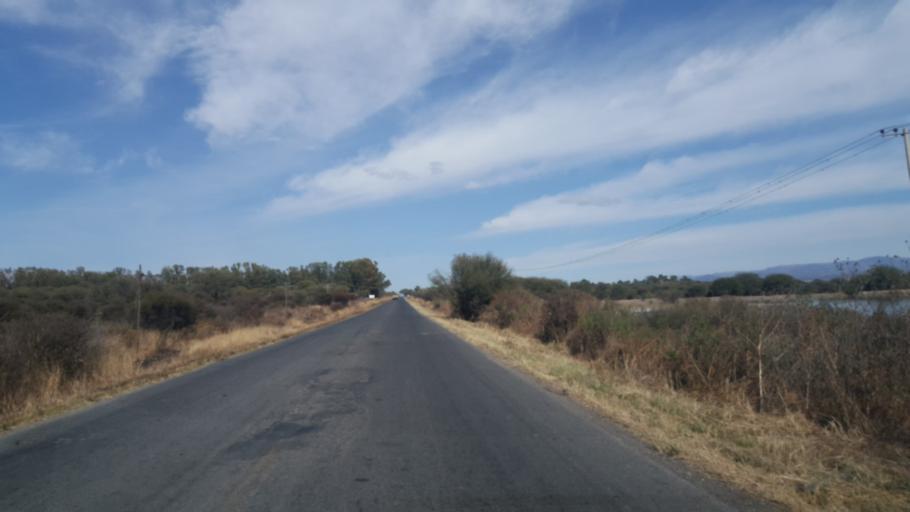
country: MX
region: Jalisco
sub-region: Lagos de Moreno
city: Cristeros [Fraccionamiento]
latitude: 21.2731
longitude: -101.9407
